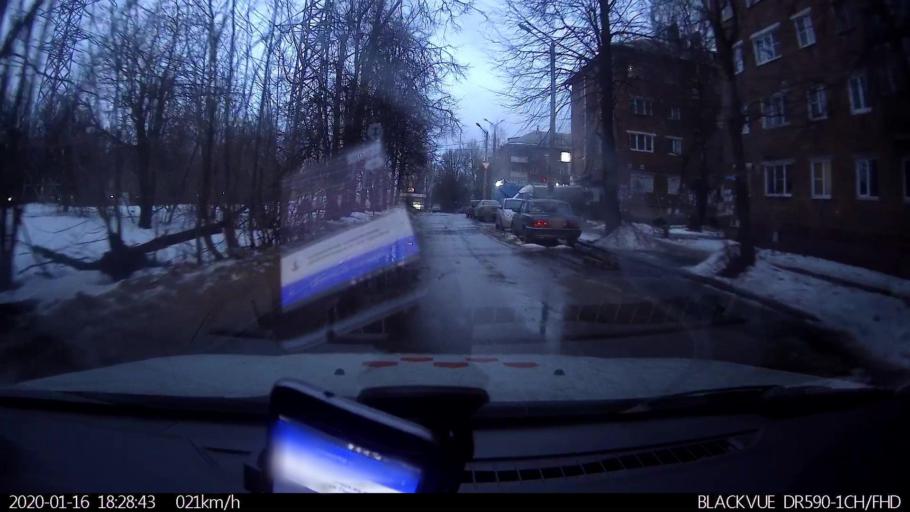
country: RU
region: Nizjnij Novgorod
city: Nizhniy Novgorod
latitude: 56.2937
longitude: 44.0134
